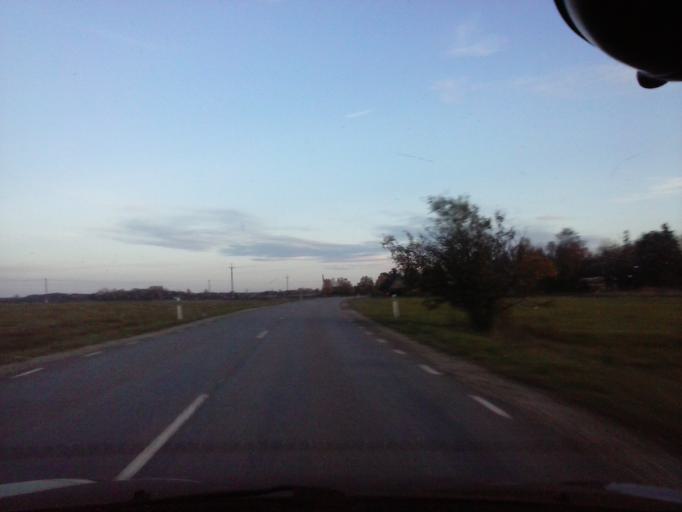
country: EE
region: Raplamaa
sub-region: Maerjamaa vald
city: Marjamaa
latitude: 58.9223
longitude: 24.4074
